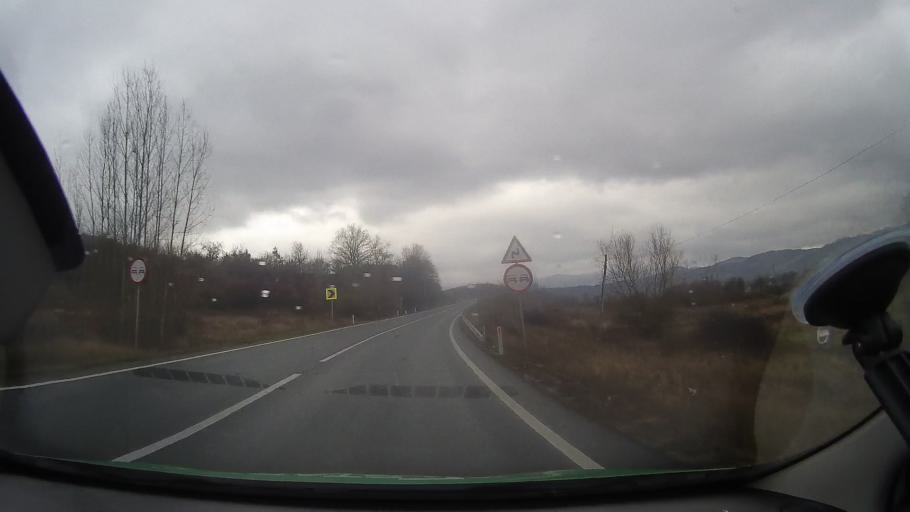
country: RO
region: Hunedoara
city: Vata de Jos
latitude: 46.2120
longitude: 22.5799
